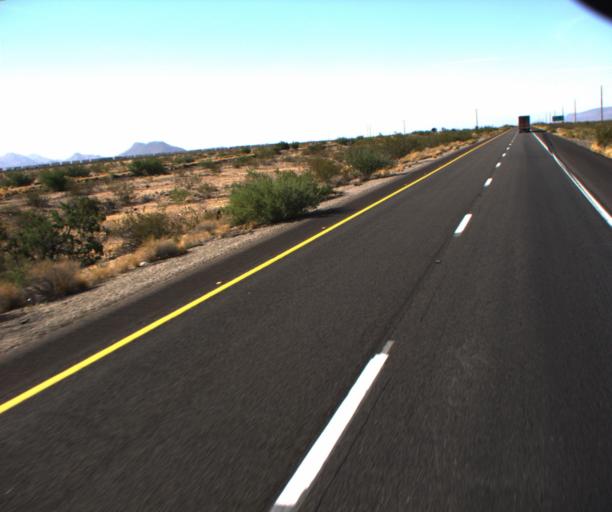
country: US
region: Arizona
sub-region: Mohave County
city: Kingman
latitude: 35.0222
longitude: -114.1329
